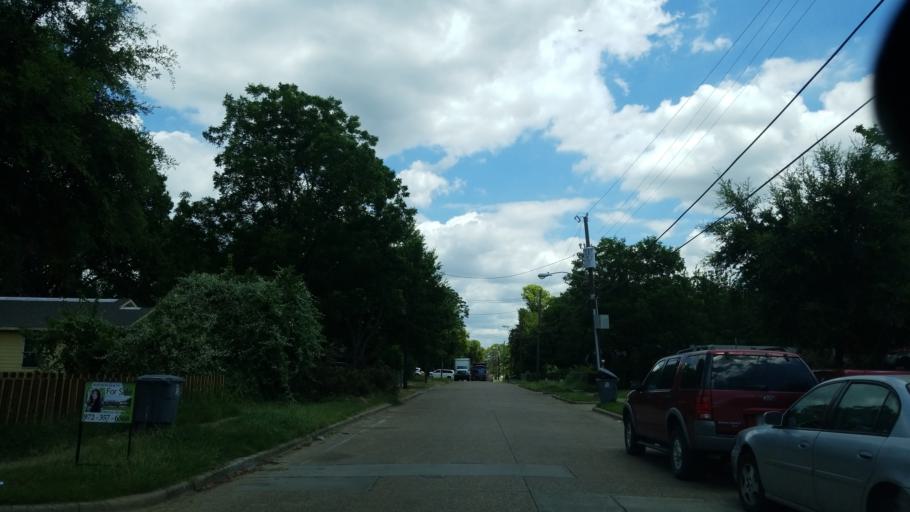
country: US
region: Texas
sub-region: Dallas County
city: Dallas
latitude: 32.7427
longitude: -96.7506
